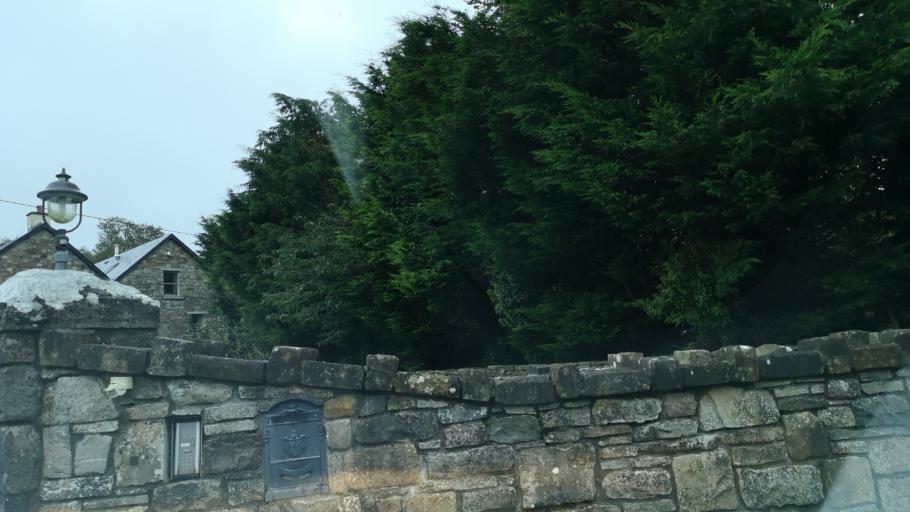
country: IE
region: Connaught
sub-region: Roscommon
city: Ballaghaderreen
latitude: 53.8963
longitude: -8.6019
